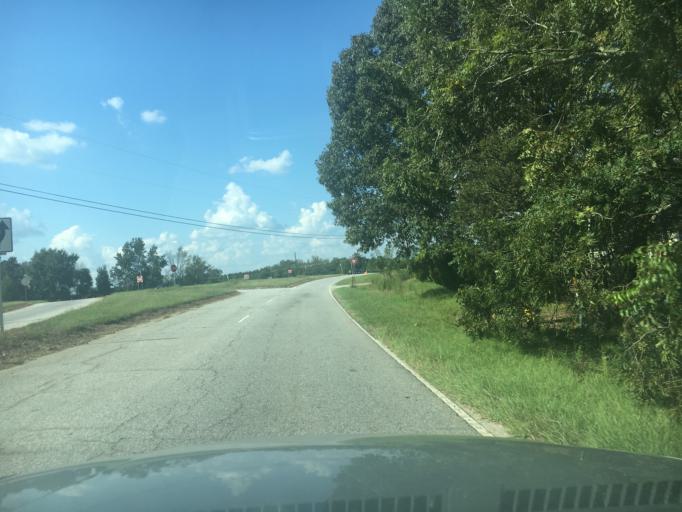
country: US
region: South Carolina
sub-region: Greenwood County
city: Ware Shoals
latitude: 34.3002
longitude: -82.2215
